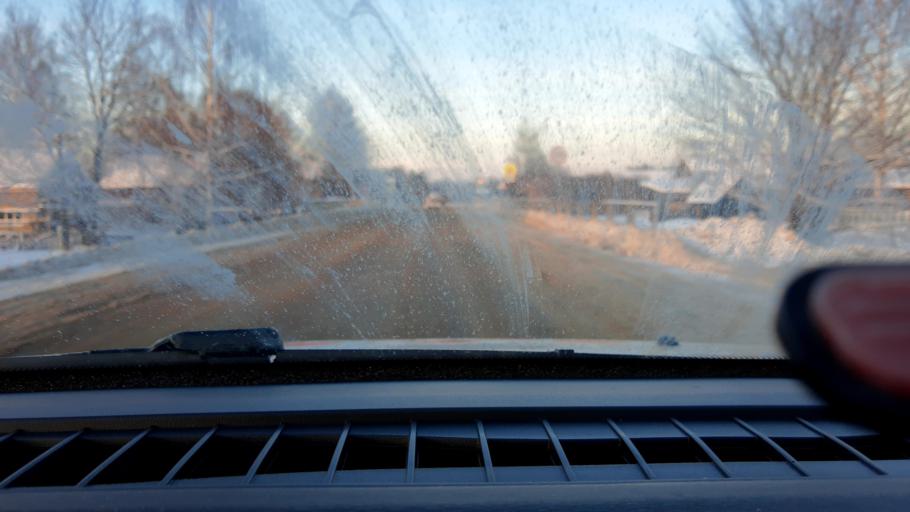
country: RU
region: Nizjnij Novgorod
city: Prudy
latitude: 57.4005
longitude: 46.0839
